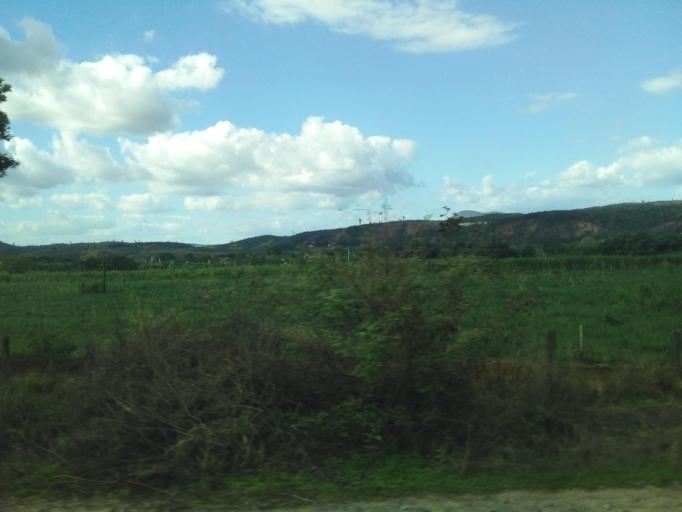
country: BR
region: Minas Gerais
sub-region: Conselheiro Pena
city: Conselheiro Pena
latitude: -18.9838
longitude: -41.6070
